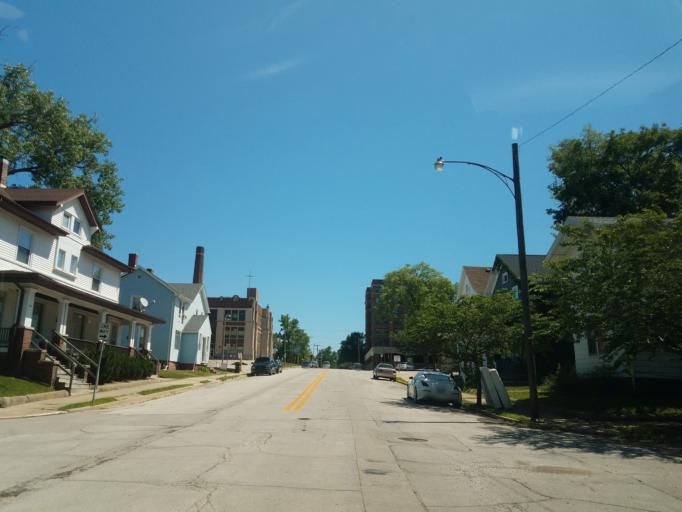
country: US
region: Illinois
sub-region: McLean County
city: Bloomington
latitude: 40.4813
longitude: -88.9886
